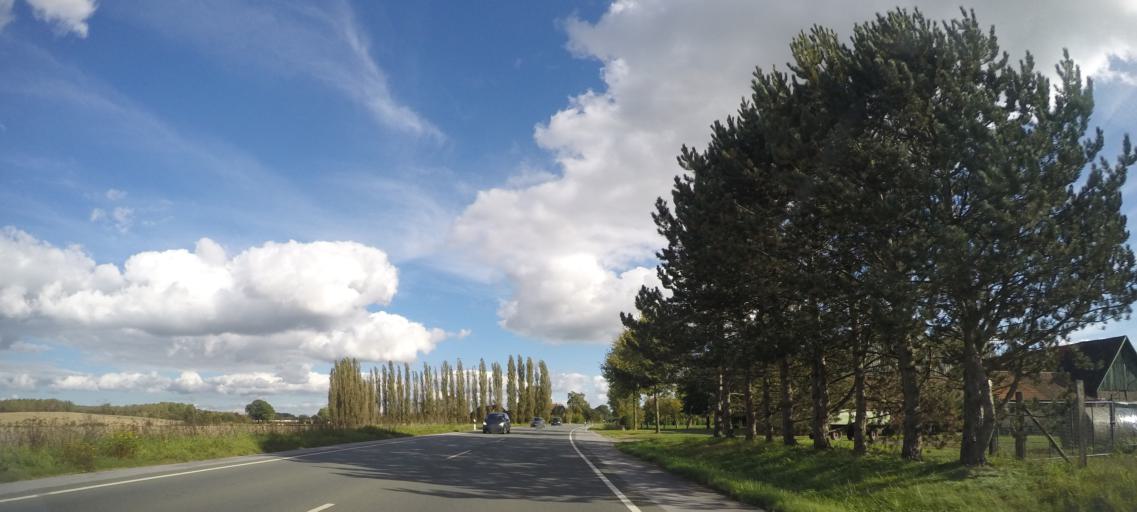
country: DE
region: North Rhine-Westphalia
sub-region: Regierungsbezirk Arnsberg
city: Welver
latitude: 51.6906
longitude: 7.9838
